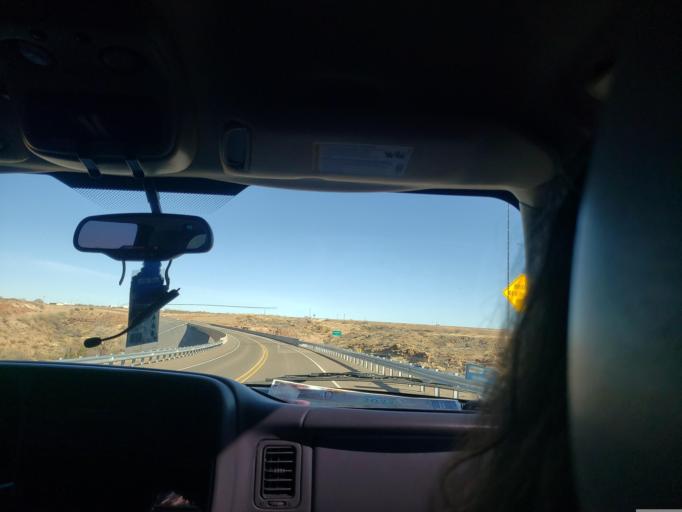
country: US
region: New Mexico
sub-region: Quay County
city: Logan
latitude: 35.3533
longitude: -103.4153
